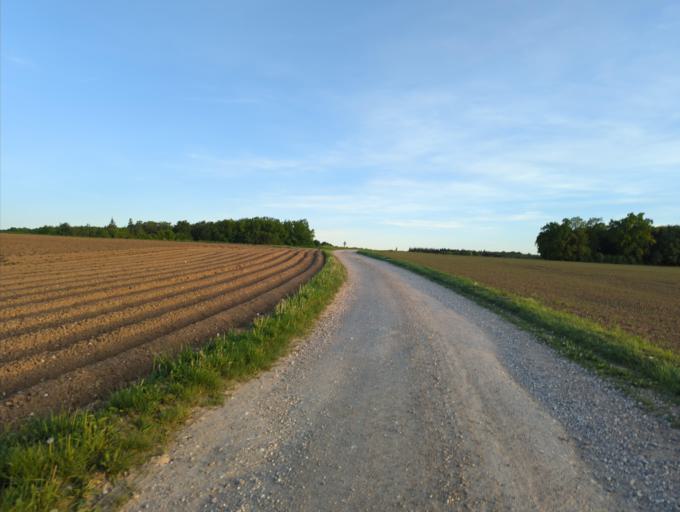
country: DE
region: Bavaria
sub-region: Upper Palatinate
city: Alteglofsheim
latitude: 48.9158
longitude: 12.1895
